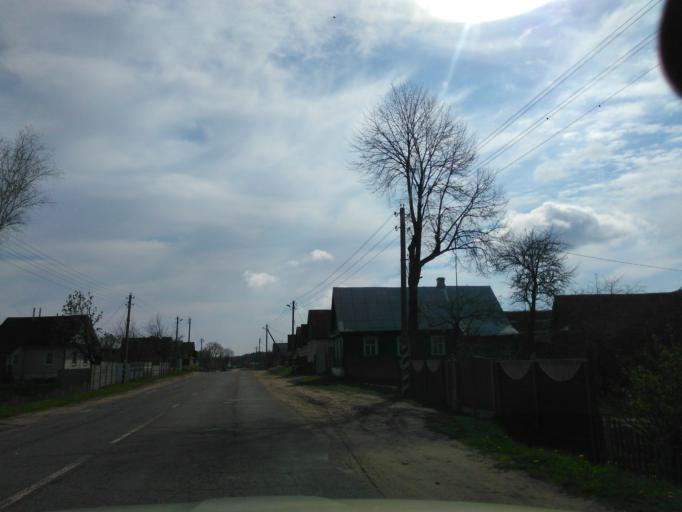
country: BY
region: Minsk
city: Rakaw
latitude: 53.9670
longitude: 27.0619
